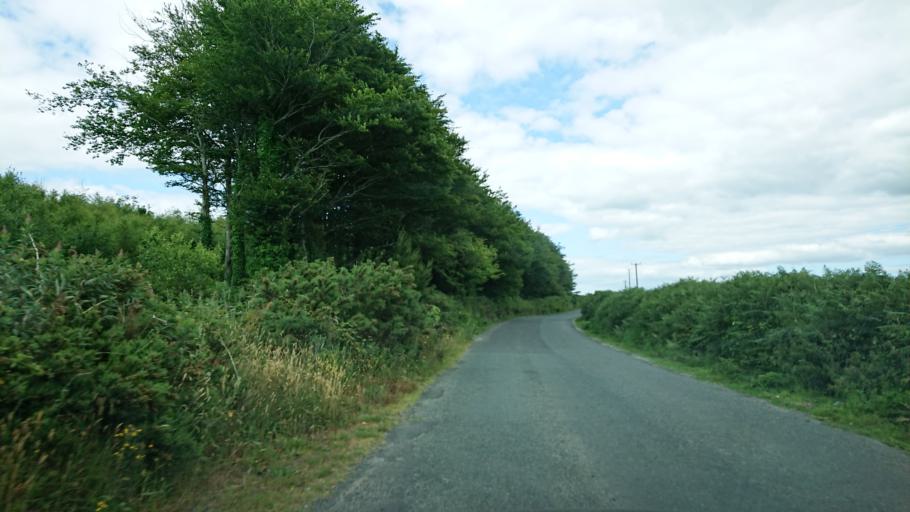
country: IE
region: Munster
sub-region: Waterford
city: Tra Mhor
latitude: 52.2096
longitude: -7.1715
